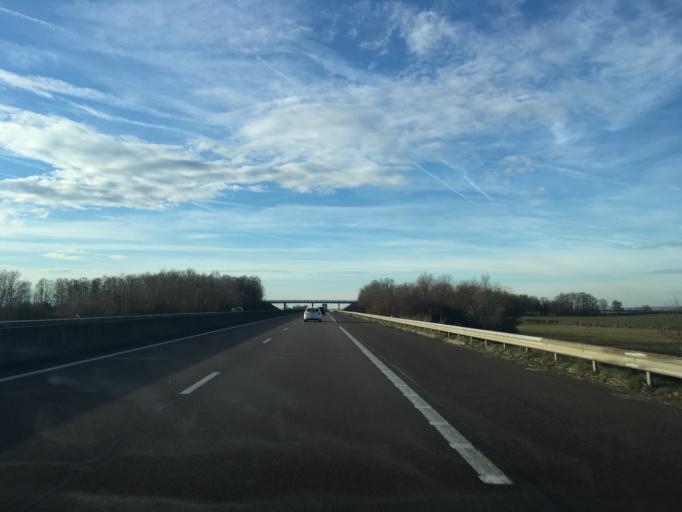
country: FR
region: Bourgogne
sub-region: Departement de la Cote-d'Or
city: Semur-en-Auxois
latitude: 47.4723
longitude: 4.2155
